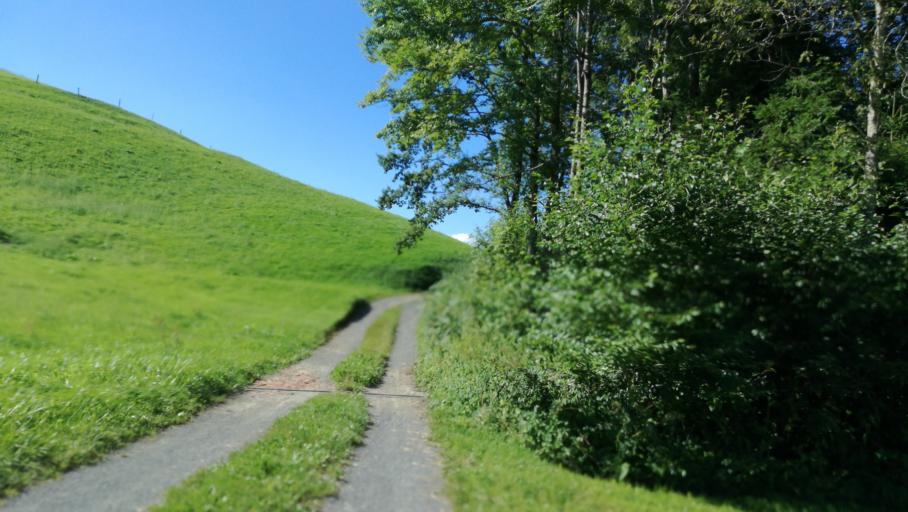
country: CH
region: Zug
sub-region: Zug
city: Unterageri
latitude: 47.1569
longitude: 8.5555
